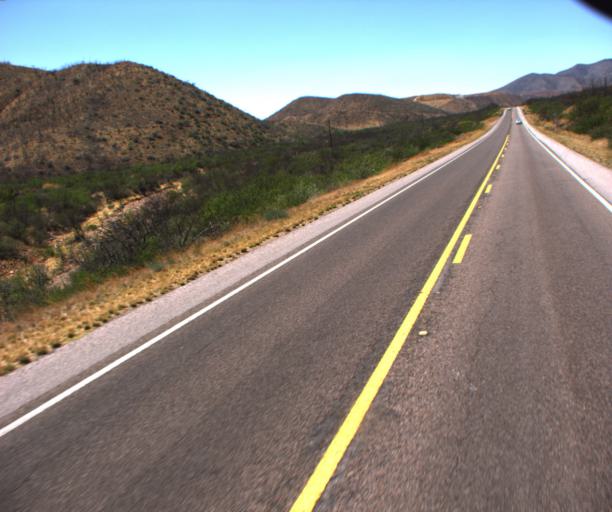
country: US
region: Arizona
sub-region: Cochise County
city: Bisbee
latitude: 31.4328
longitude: -109.8465
